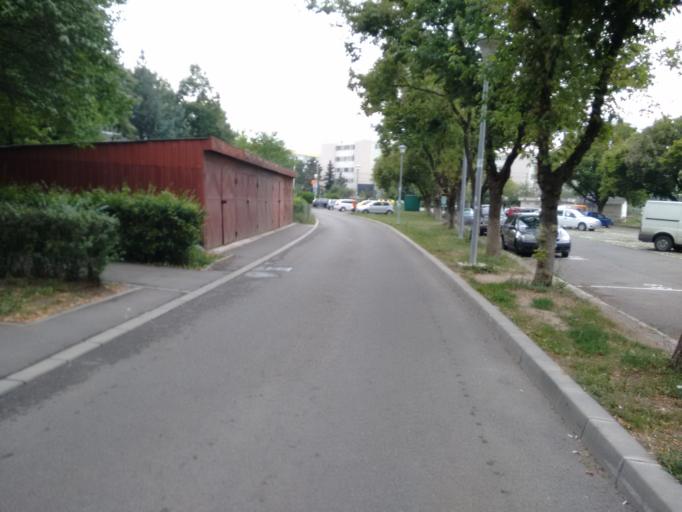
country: RO
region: Cluj
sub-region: Municipiul Cluj-Napoca
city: Cluj-Napoca
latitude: 46.7673
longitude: 23.6305
